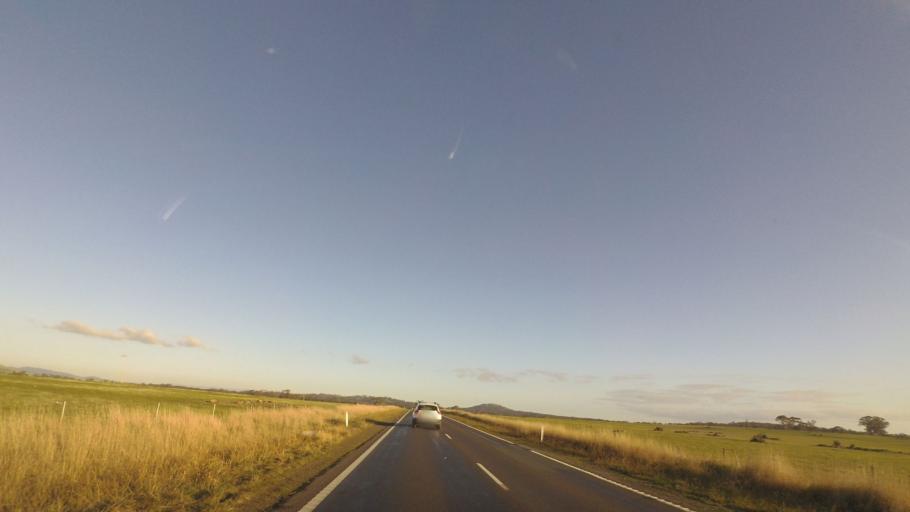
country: AU
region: Victoria
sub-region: Mount Alexander
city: Castlemaine
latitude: -37.1399
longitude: 144.5078
